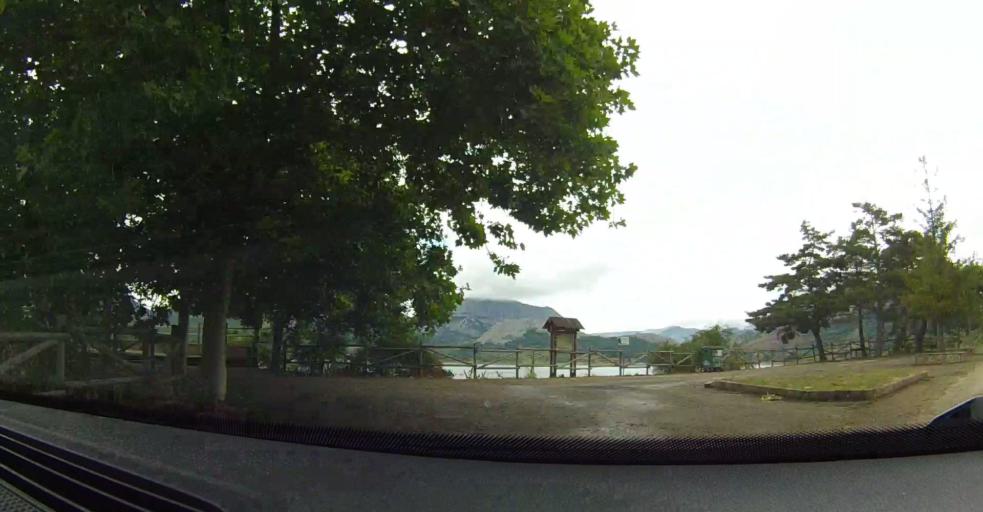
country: ES
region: Castille and Leon
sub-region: Provincia de Leon
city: Puebla de Lillo
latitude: 42.9344
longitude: -5.2810
